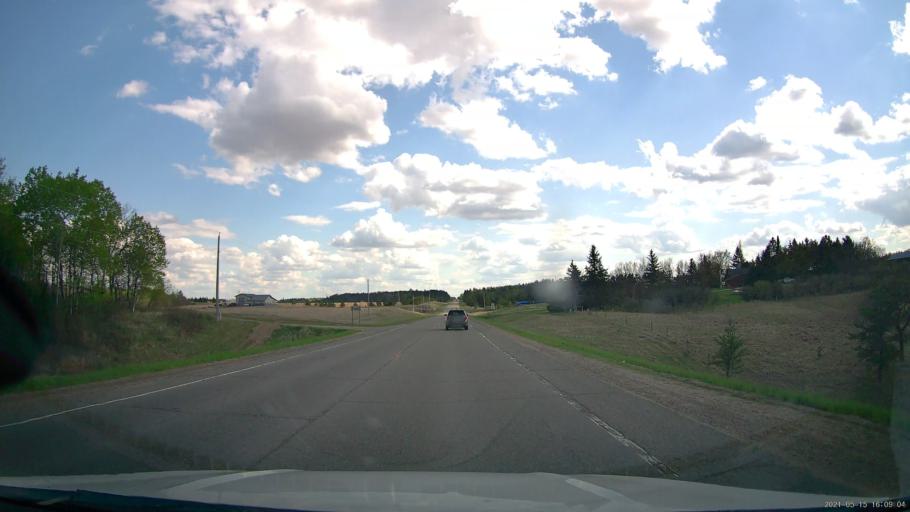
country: US
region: Minnesota
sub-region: Hubbard County
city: Park Rapids
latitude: 46.9543
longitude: -94.9527
